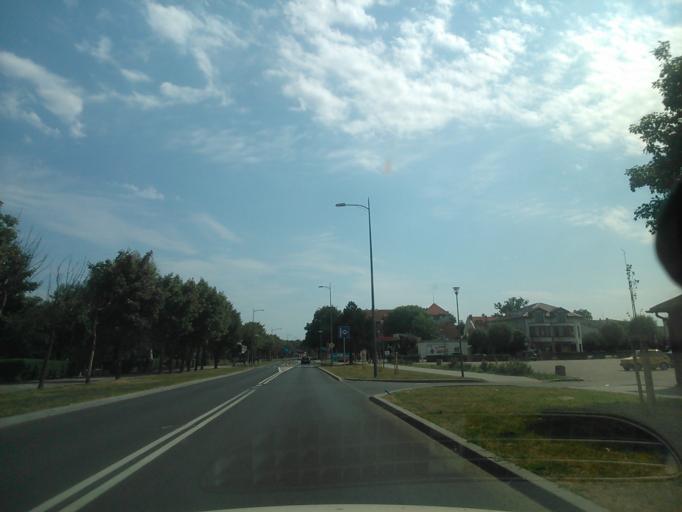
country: PL
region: Warmian-Masurian Voivodeship
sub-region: Powiat dzialdowski
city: Dzialdowo
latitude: 53.2361
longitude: 20.1789
